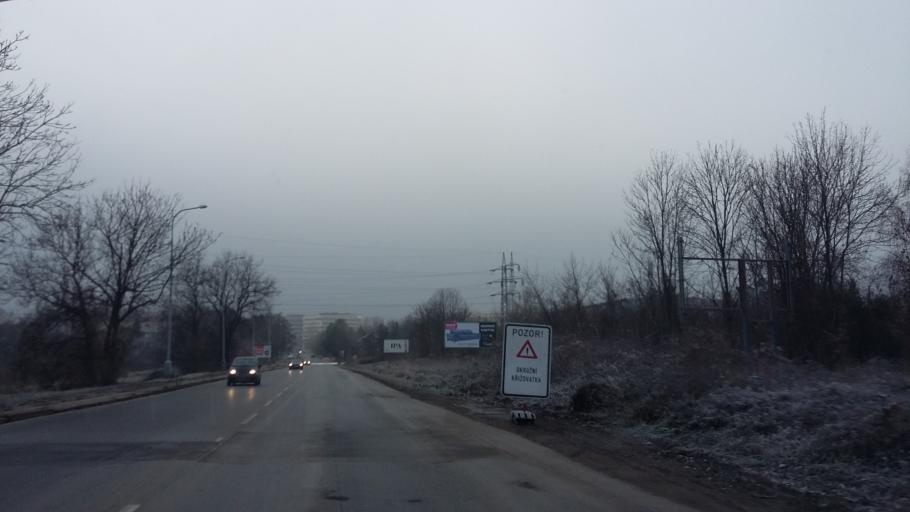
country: CZ
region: Praha
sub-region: Praha 9
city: Prosek
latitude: 50.1187
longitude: 14.5121
